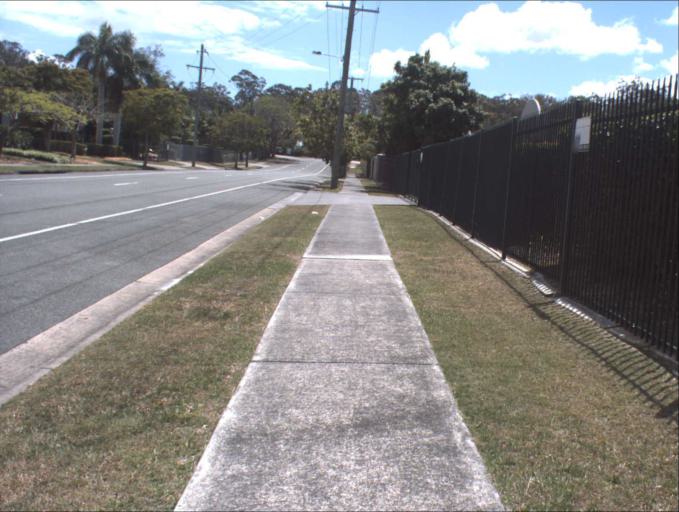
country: AU
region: Queensland
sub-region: Logan
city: Slacks Creek
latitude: -27.6541
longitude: 153.1674
